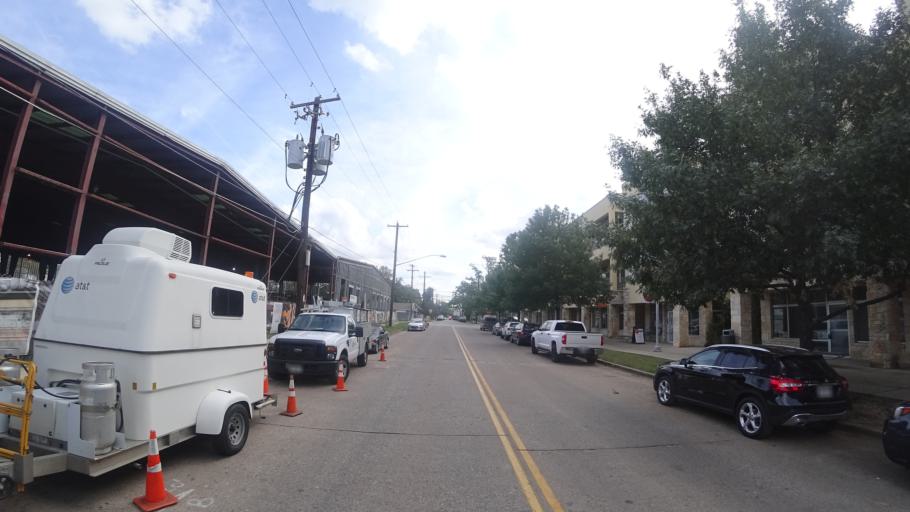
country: US
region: Texas
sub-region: Travis County
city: Austin
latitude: 30.2592
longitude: -97.7154
